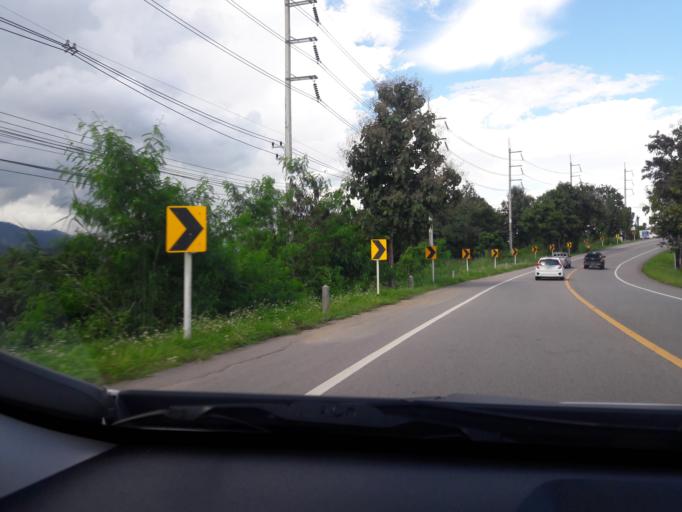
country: TH
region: Mae Hong Son
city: Mae Hi
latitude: 19.3358
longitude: 98.4316
